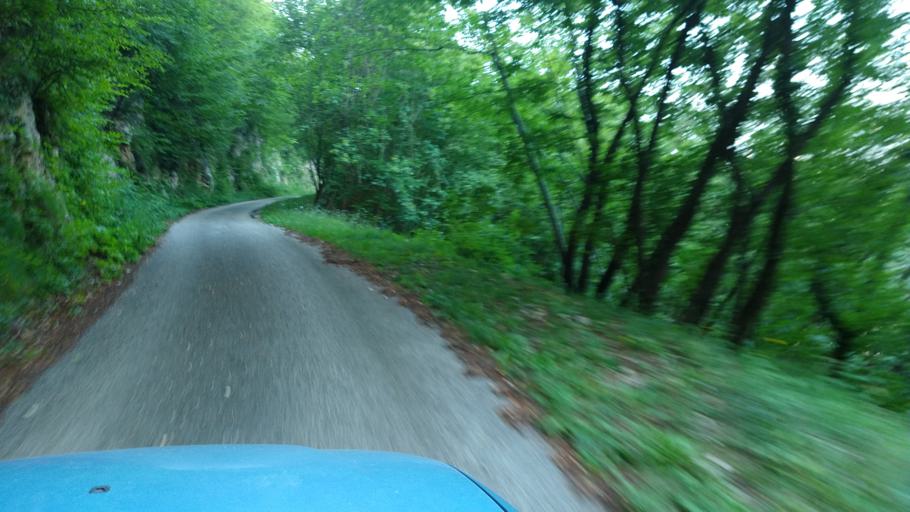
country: IT
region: Veneto
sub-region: Provincia di Vicenza
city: Campolongo sul Brenta
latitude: 45.8263
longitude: 11.6876
